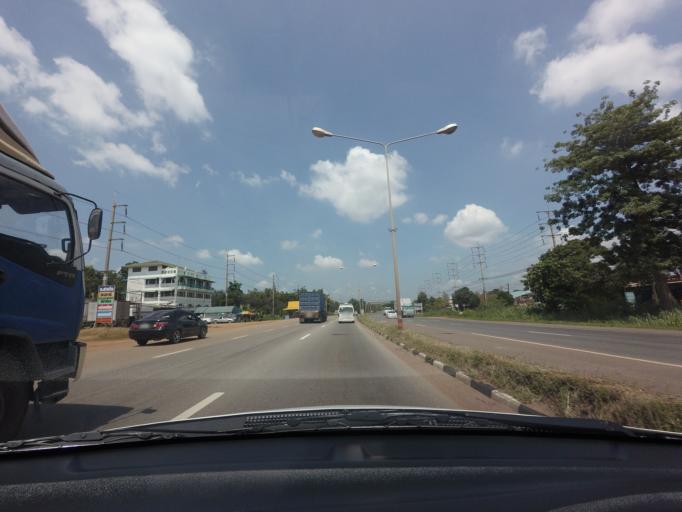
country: TH
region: Prachin Buri
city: Si Maha Phot
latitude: 13.8622
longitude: 101.5550
